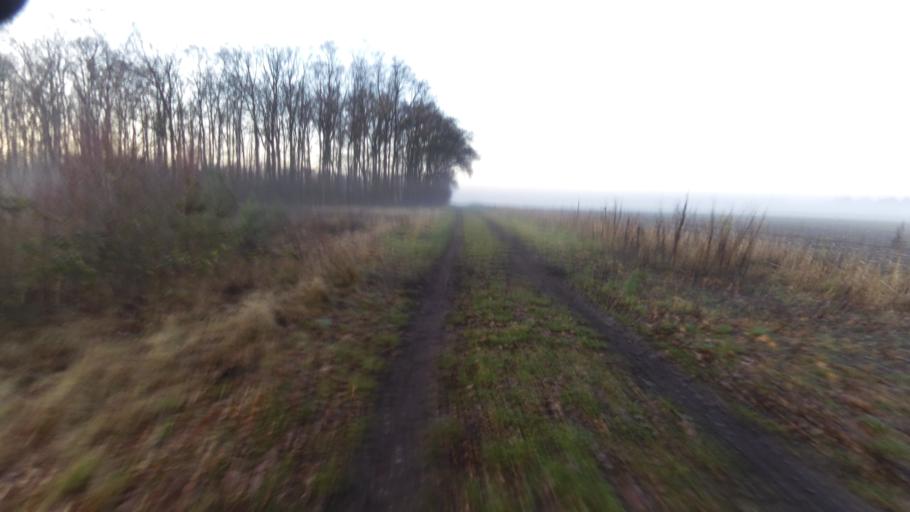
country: NL
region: Gelderland
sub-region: Gemeente Apeldoorn
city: Uddel
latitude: 52.2397
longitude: 5.7889
